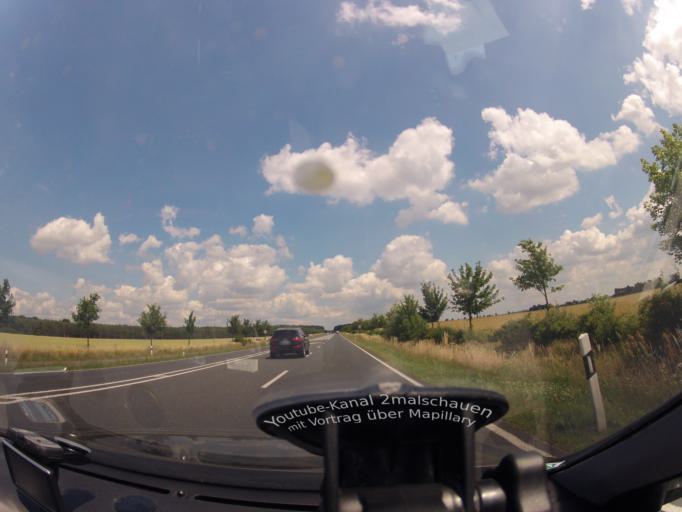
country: DE
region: Saxony
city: Mockrehna
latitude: 51.5150
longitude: 12.8375
